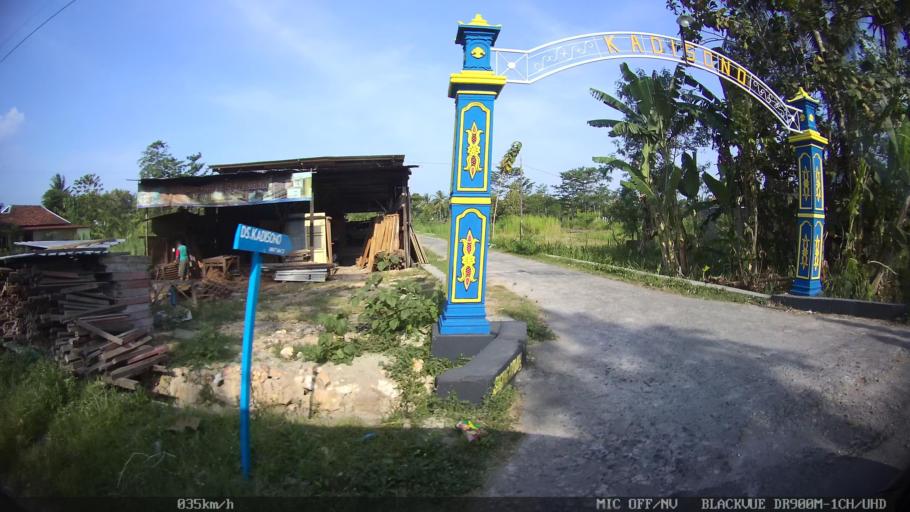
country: ID
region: Daerah Istimewa Yogyakarta
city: Bantul
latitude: -7.8834
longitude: 110.3054
